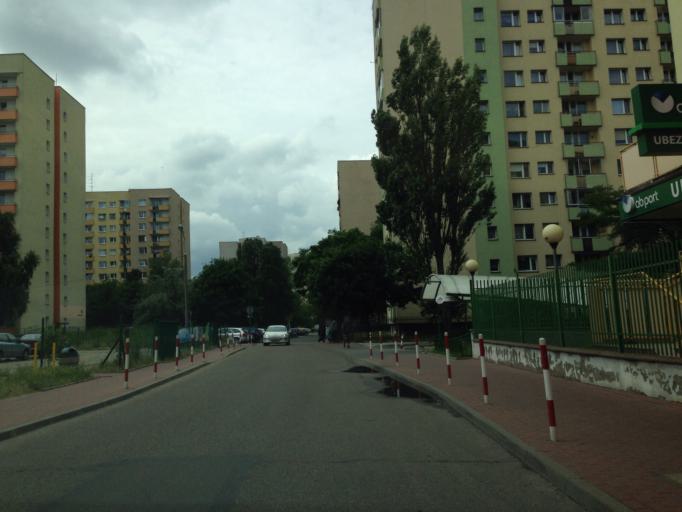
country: PL
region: Masovian Voivodeship
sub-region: Warszawa
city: Bemowo
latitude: 52.2566
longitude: 20.9278
